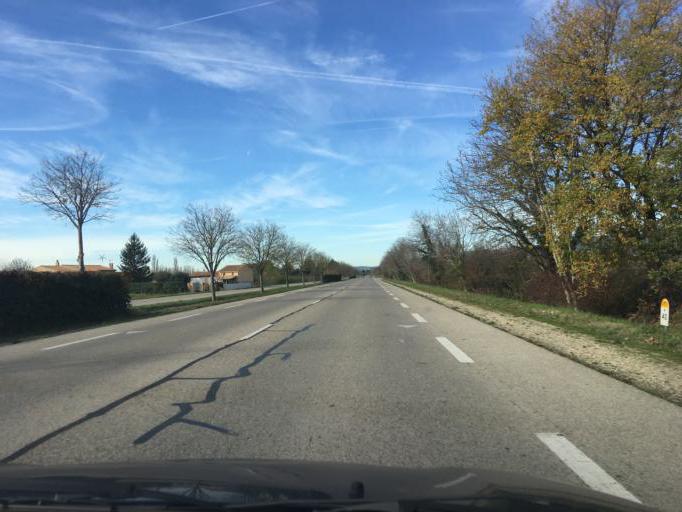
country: FR
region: Provence-Alpes-Cote d'Azur
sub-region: Departement du Vaucluse
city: Cadenet
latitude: 43.7323
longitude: 5.3581
